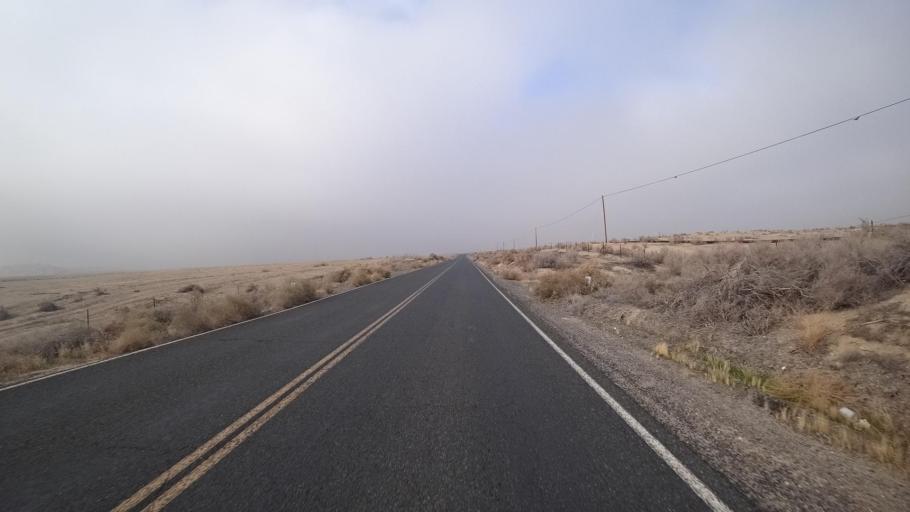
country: US
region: California
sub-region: Kern County
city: Ford City
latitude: 35.2485
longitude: -119.4619
